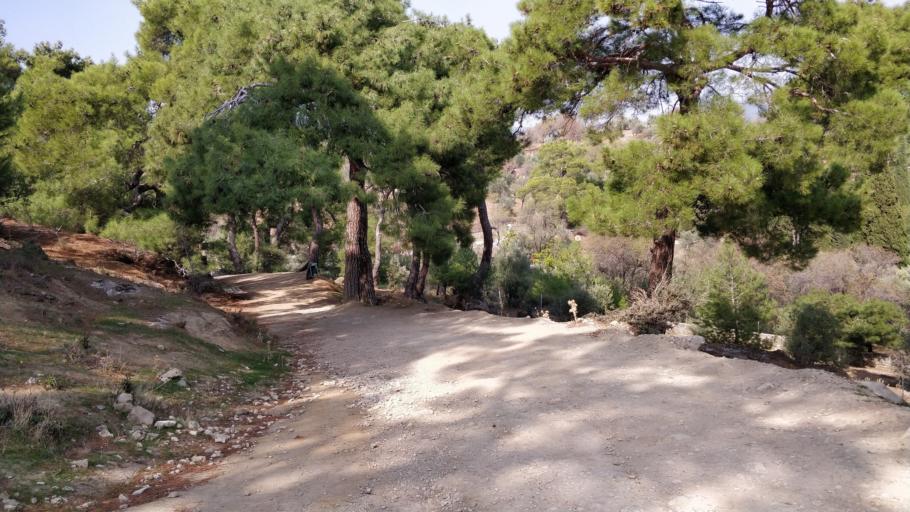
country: TR
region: Canakkale
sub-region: Merkez
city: Kucukkuyu
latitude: 39.5668
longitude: 26.6166
